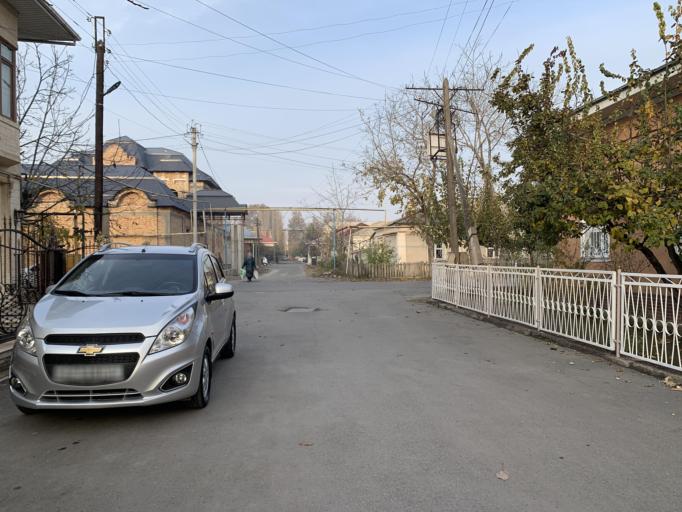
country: UZ
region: Fergana
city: Qo`qon
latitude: 40.5445
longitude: 70.9270
